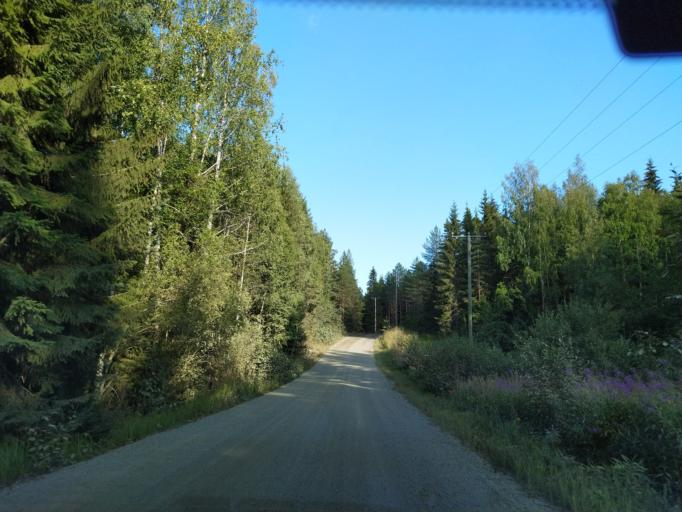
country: FI
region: Central Finland
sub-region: Jaemsae
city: Kuhmoinen
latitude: 61.6904
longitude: 24.9561
